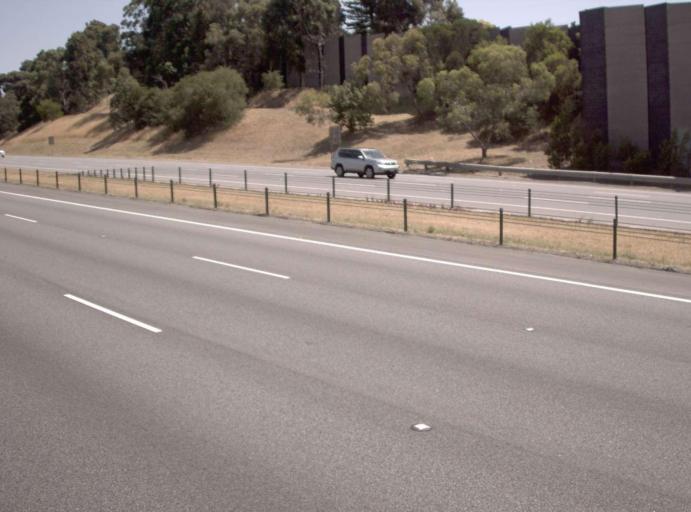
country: AU
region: Victoria
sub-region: Monash
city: Chadstone
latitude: -37.8910
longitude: 145.1183
